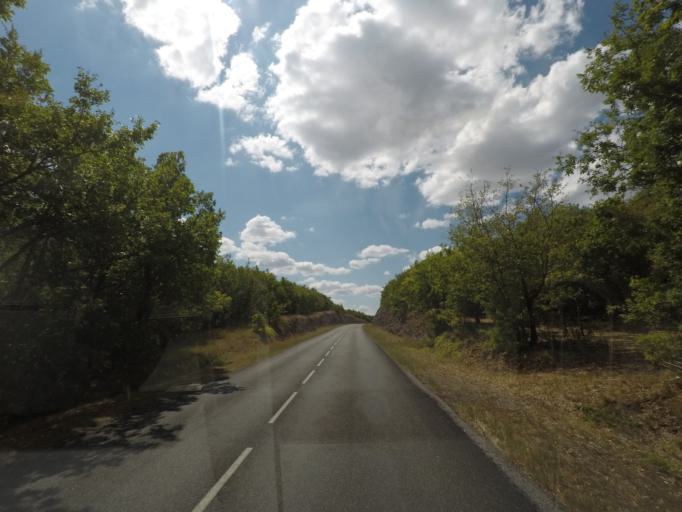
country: FR
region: Midi-Pyrenees
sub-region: Departement du Lot
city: Cajarc
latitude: 44.5776
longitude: 1.6899
